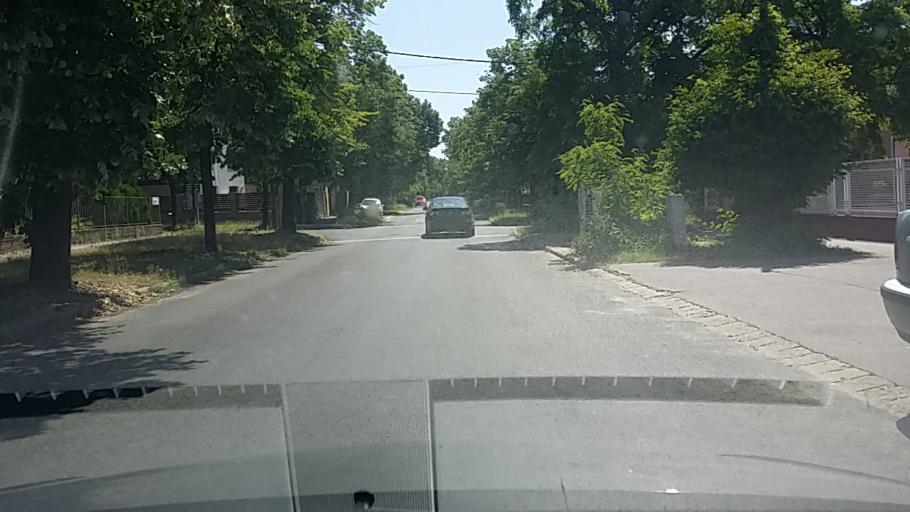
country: HU
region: Budapest
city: Budapest XIV. keruelet
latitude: 47.5243
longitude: 19.1344
